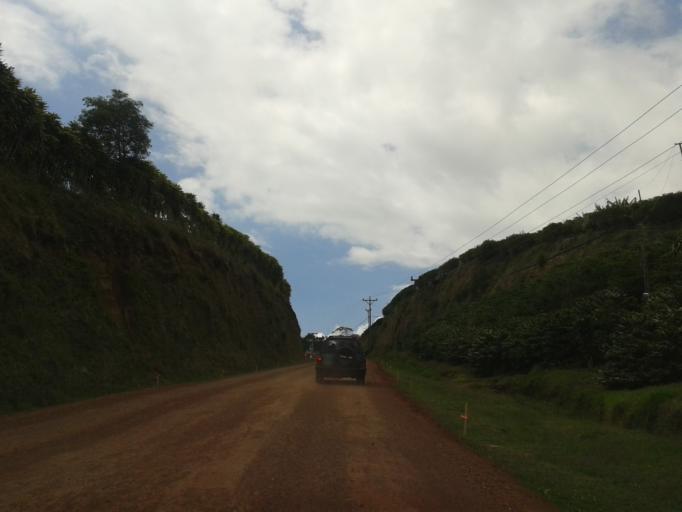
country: CR
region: Alajuela
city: Sabanilla
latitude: 10.0922
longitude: -84.1887
